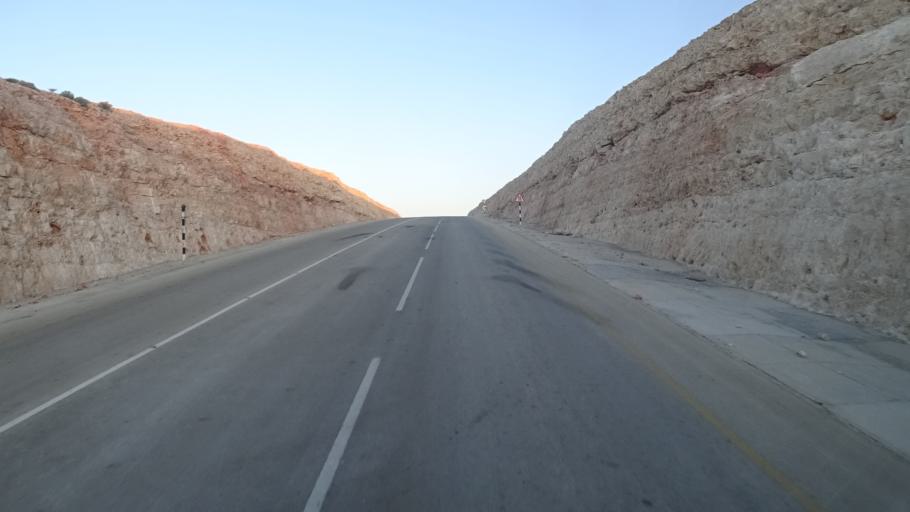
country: YE
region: Al Mahrah
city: Hawf
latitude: 16.9522
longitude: 53.3442
